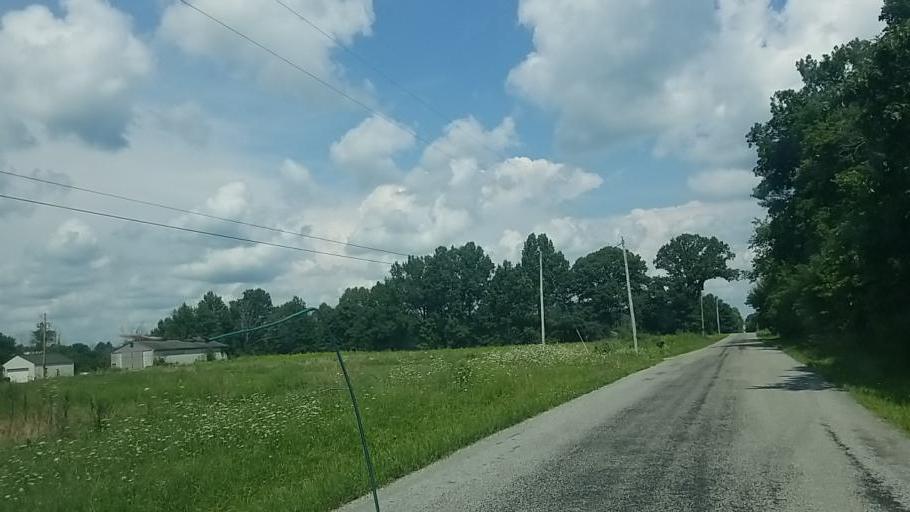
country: US
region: Ohio
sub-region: Wayne County
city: West Salem
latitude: 41.0082
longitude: -82.0781
